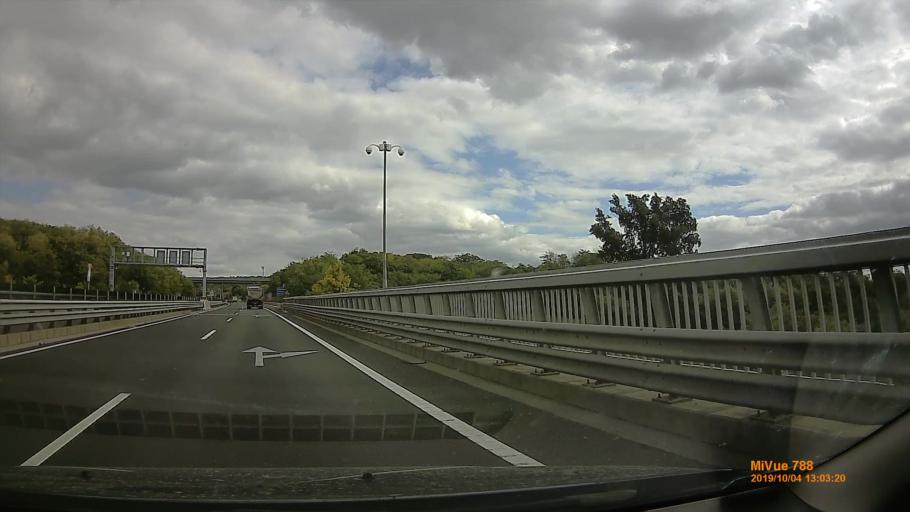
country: HU
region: Somogy
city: Balatonfoldvar
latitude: 46.8160
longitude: 17.9133
